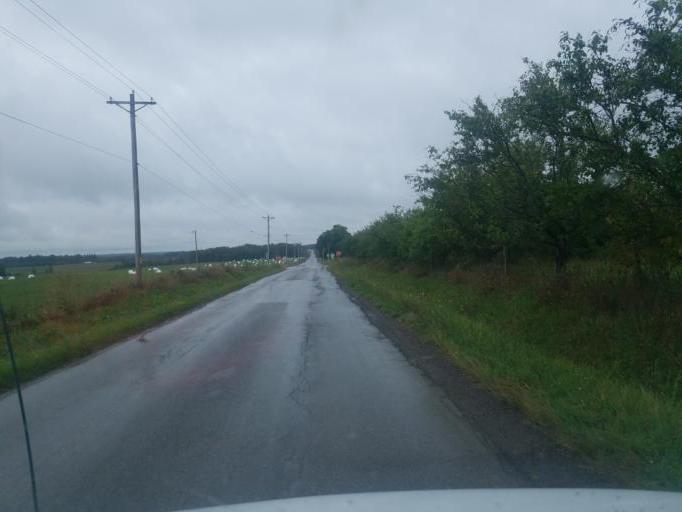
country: US
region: Ohio
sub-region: Wayne County
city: West Salem
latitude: 40.9327
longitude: -82.0817
